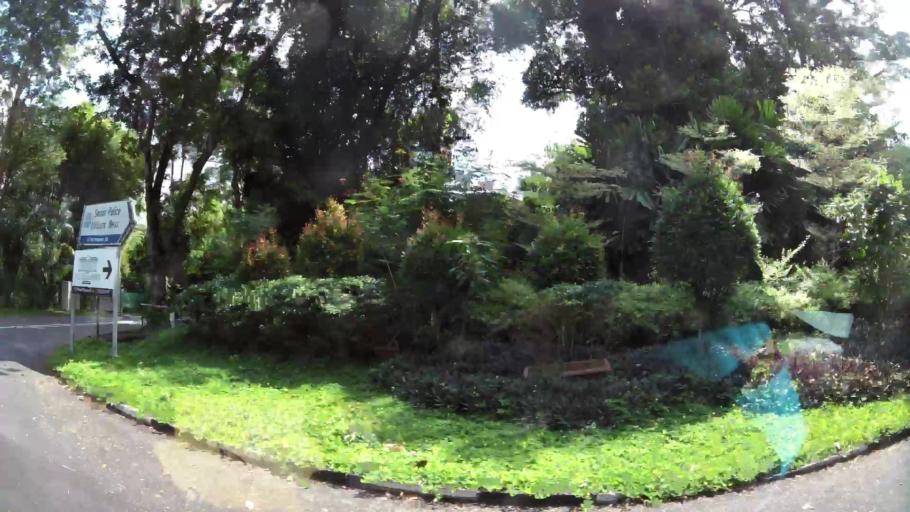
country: SG
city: Singapore
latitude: 1.3330
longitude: 103.8336
